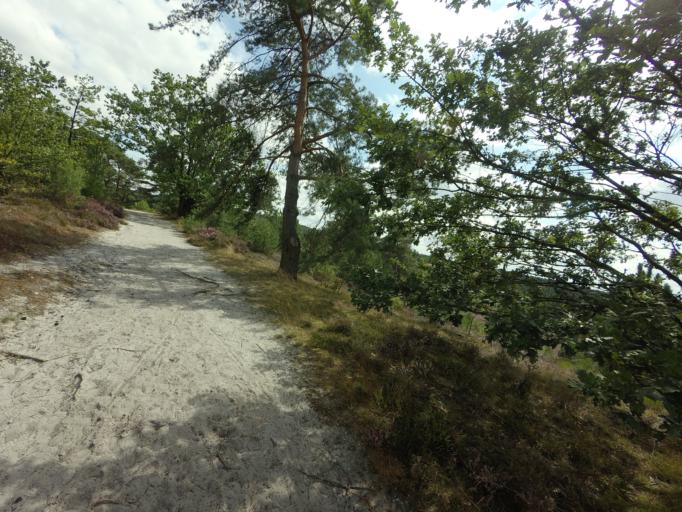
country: NL
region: Limburg
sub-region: Gemeente Brunssum
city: Brunssum
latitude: 50.9267
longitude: 6.0051
